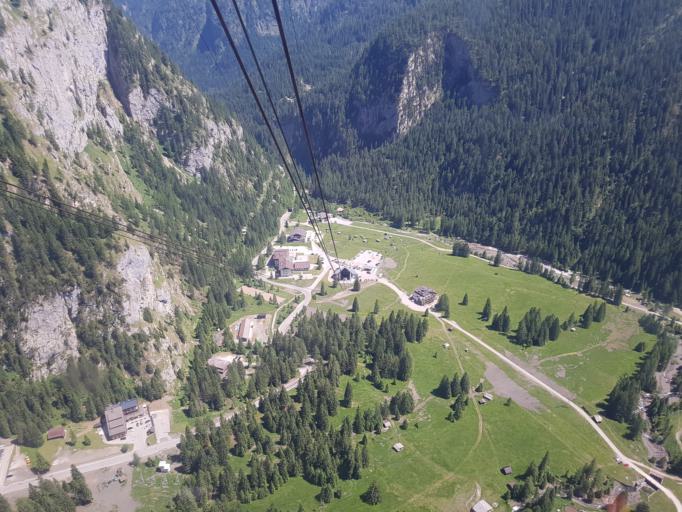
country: IT
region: Veneto
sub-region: Provincia di Belluno
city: Sachet
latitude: 46.4313
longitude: 11.9037
